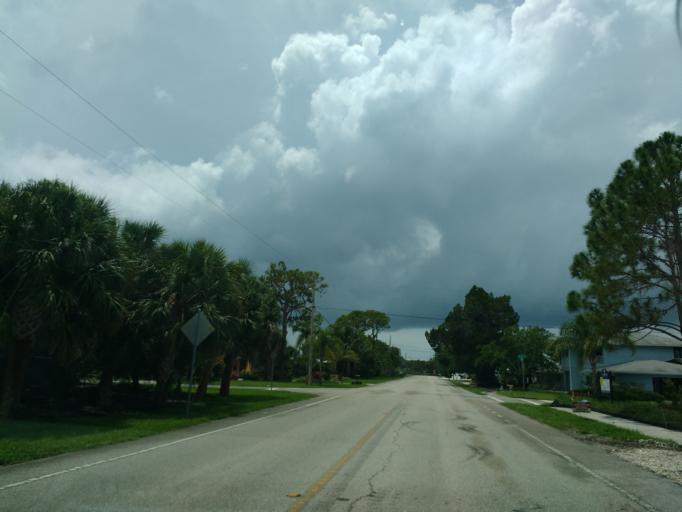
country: US
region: Florida
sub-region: Sarasota County
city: Venice
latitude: 27.0815
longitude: -82.4502
